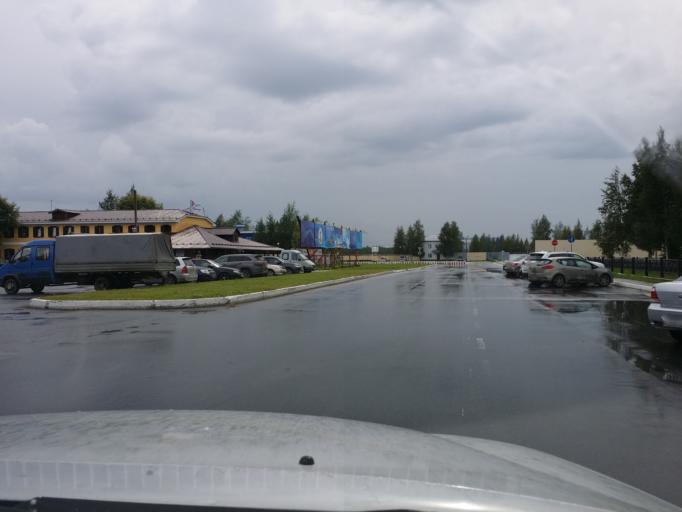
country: RU
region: Khanty-Mansiyskiy Avtonomnyy Okrug
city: Nizhnevartovsk
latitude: 60.9498
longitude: 76.4984
